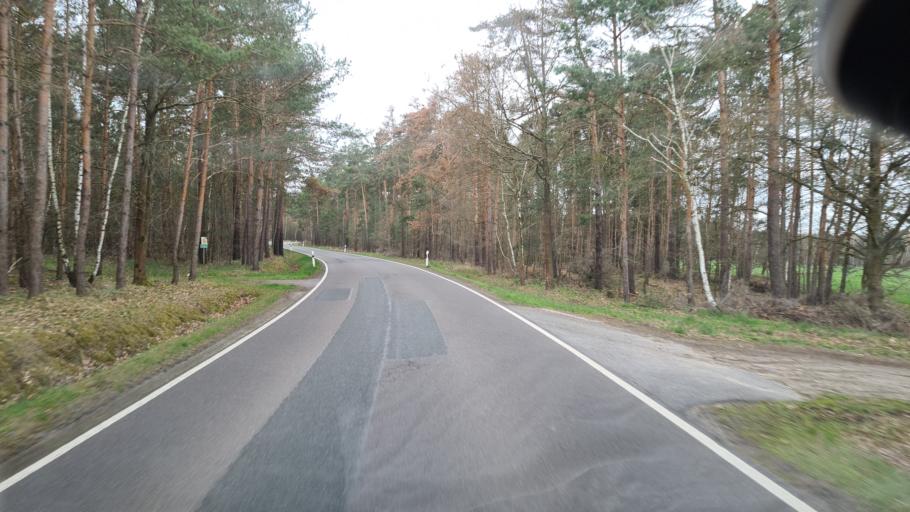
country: DE
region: Brandenburg
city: Hohenbocka
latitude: 51.4527
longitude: 13.9794
